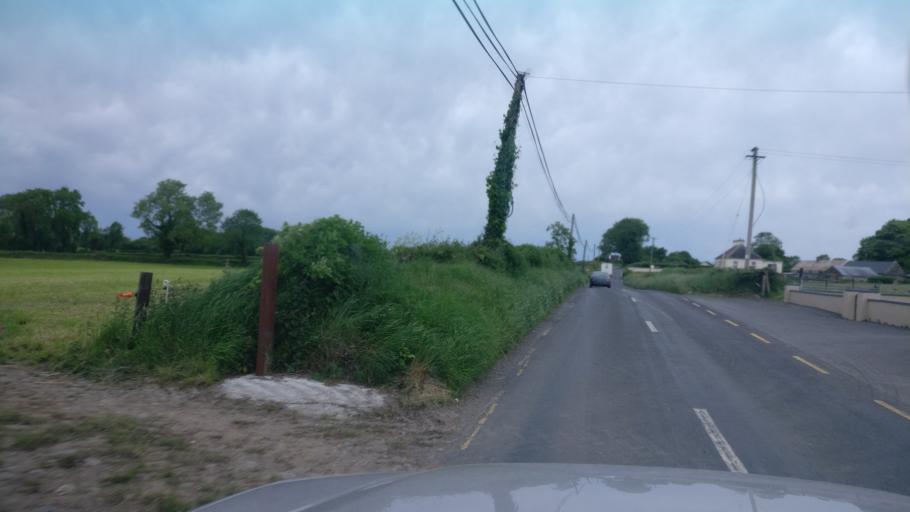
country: IE
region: Connaught
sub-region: County Galway
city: Portumna
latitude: 53.1224
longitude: -8.3257
